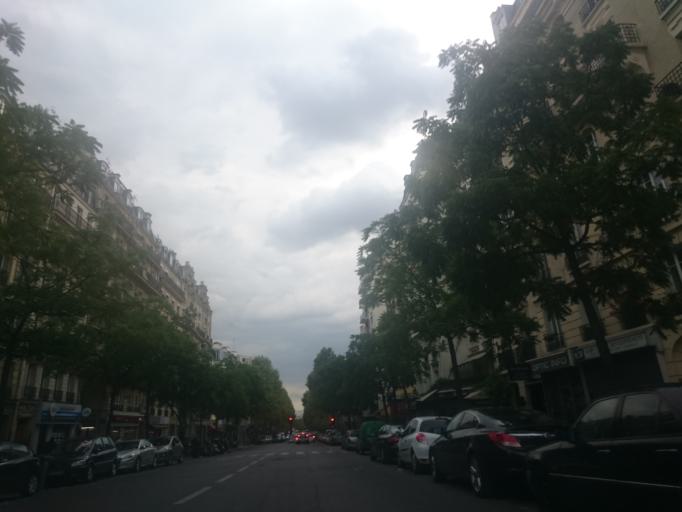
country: FR
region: Ile-de-France
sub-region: Departement du Val-de-Marne
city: Saint-Mande
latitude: 48.8491
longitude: 2.3907
